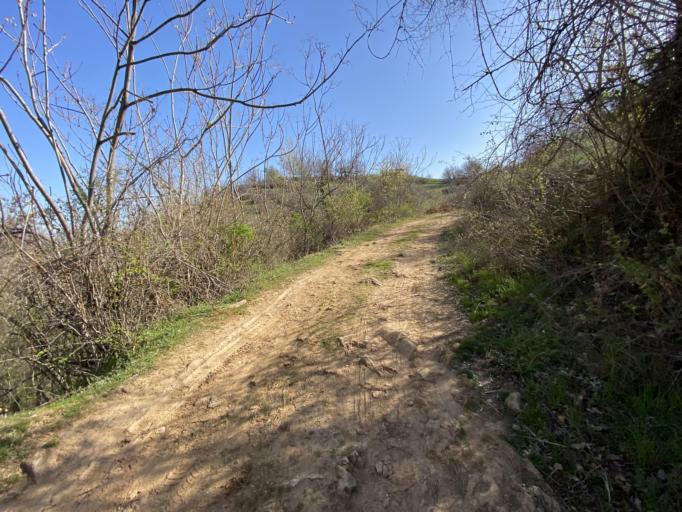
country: MK
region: Zrnovci
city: Zrnovci
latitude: 41.8455
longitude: 22.4187
